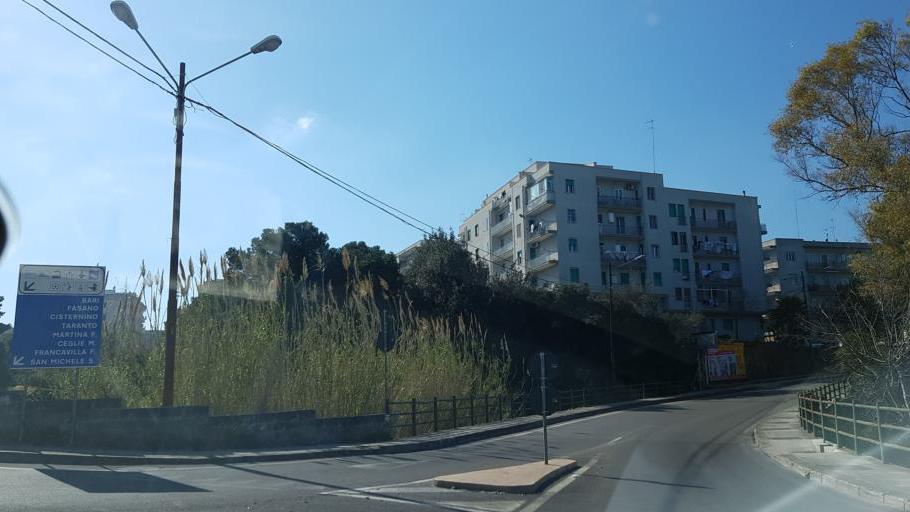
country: IT
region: Apulia
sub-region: Provincia di Brindisi
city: Ostuni
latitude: 40.7252
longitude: 17.5860
